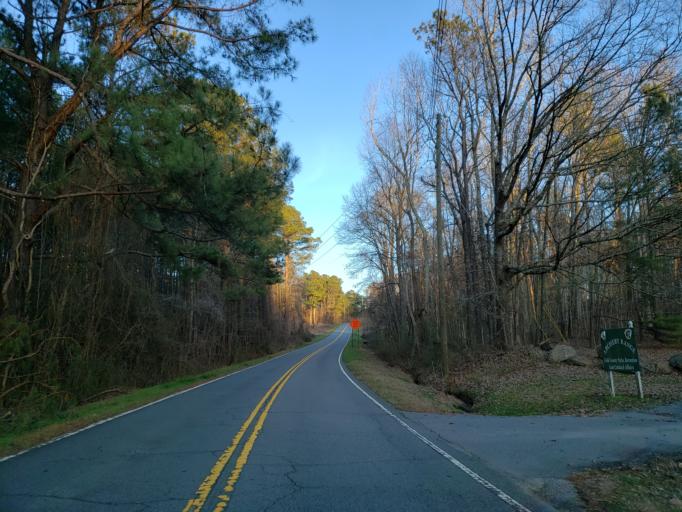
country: US
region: Georgia
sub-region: Cobb County
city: Acworth
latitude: 34.0170
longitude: -84.7318
